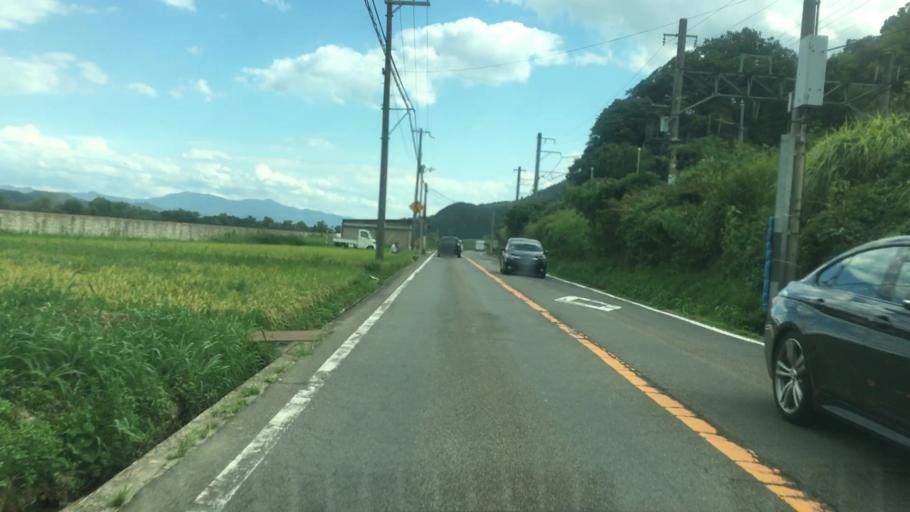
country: JP
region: Hyogo
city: Toyooka
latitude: 35.5879
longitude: 134.7997
